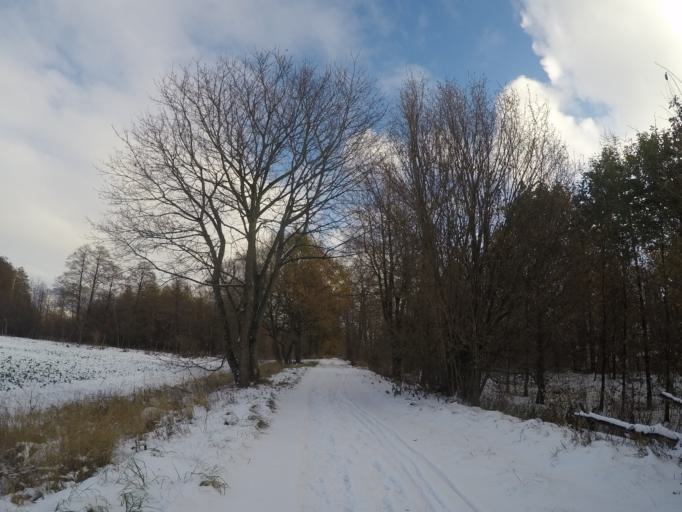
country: SE
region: Skane
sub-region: Lunds Kommun
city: Lund
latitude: 55.7852
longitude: 13.2233
